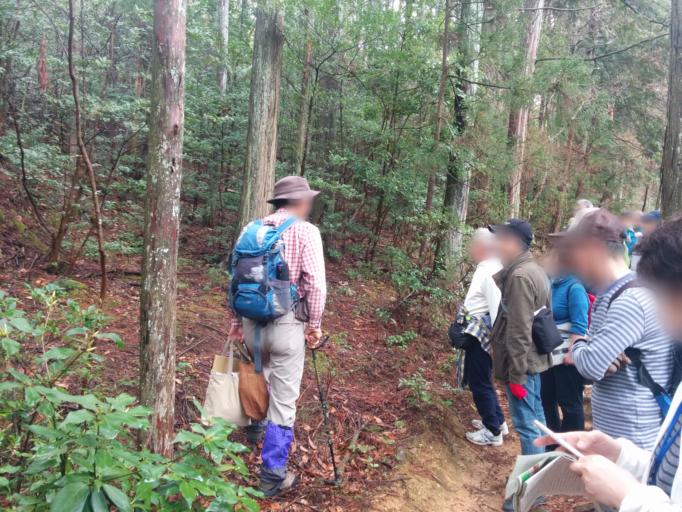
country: JP
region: Kyoto
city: Muko
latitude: 35.0392
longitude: 135.6754
